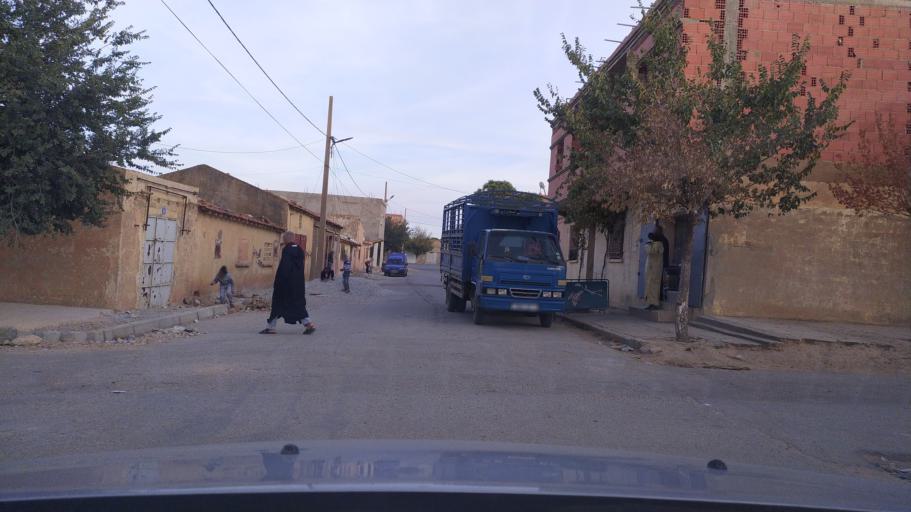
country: DZ
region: Tiaret
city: Frenda
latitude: 34.8995
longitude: 1.2359
